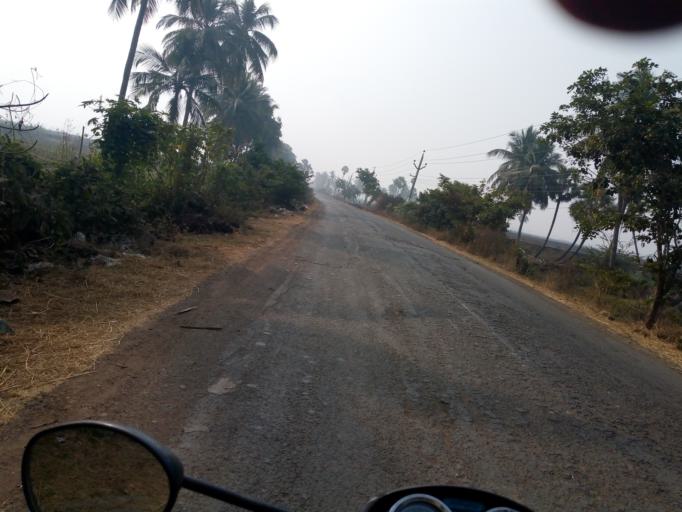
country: IN
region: Andhra Pradesh
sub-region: West Godavari
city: Tadepallegudem
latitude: 16.7432
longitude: 81.4194
